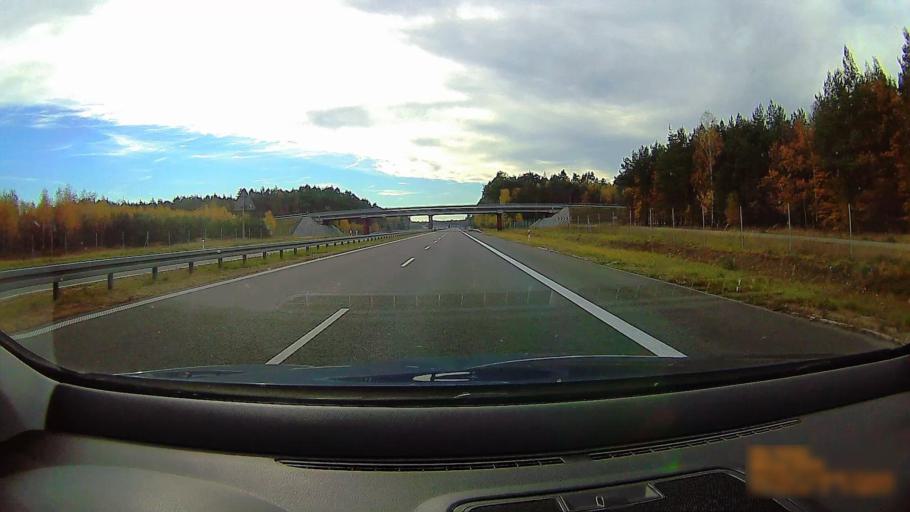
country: PL
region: Greater Poland Voivodeship
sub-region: Powiat ostrowski
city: Przygodzice
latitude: 51.5674
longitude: 17.8476
